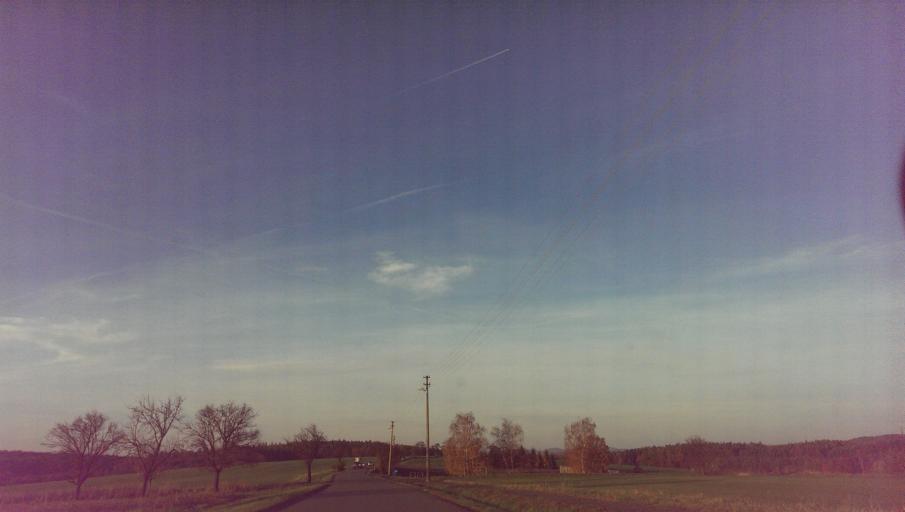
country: CZ
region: Zlin
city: Tecovice
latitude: 49.1736
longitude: 17.6050
